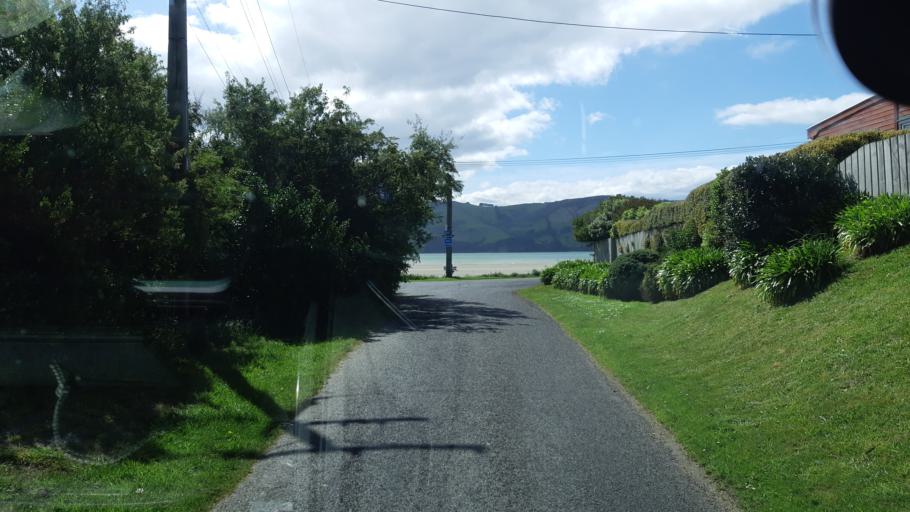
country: NZ
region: Otago
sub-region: Dunedin City
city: Portobello
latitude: -45.8131
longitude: 170.6770
